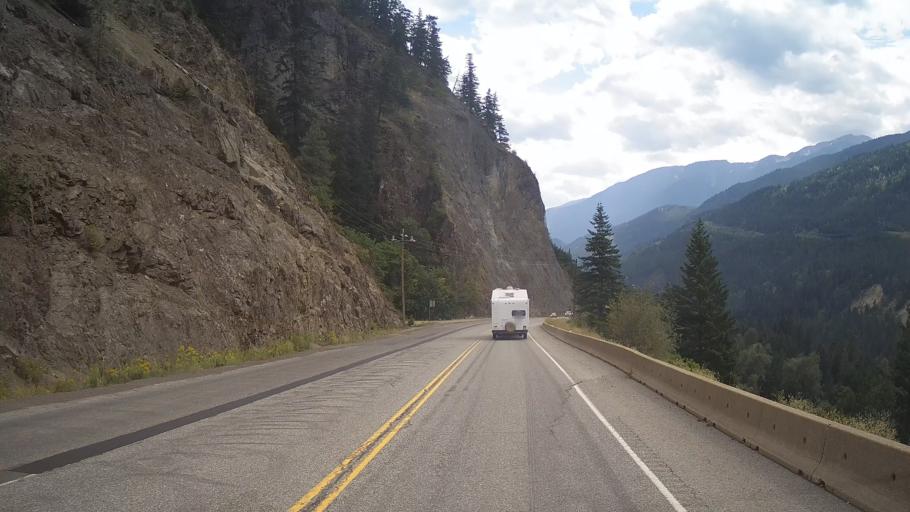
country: CA
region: British Columbia
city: Hope
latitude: 50.0674
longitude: -121.5453
